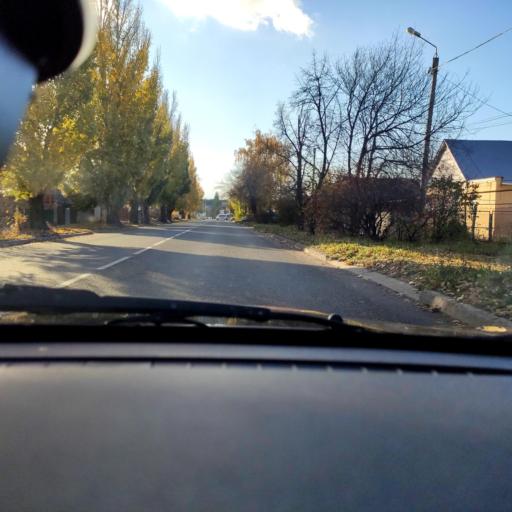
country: RU
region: Samara
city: Tol'yatti
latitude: 53.5366
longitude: 49.3999
